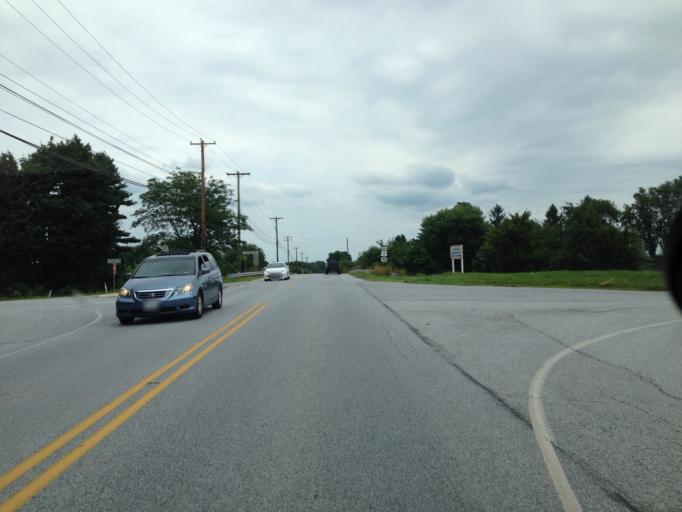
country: US
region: Pennsylvania
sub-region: Chester County
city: Oxford
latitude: 39.8216
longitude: -75.9161
